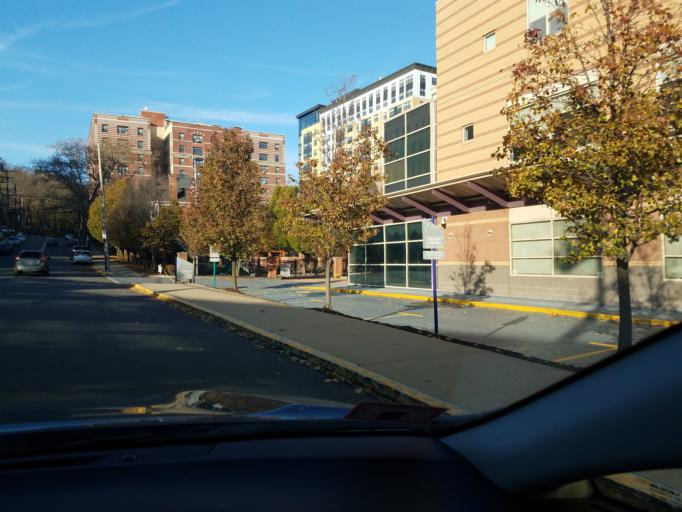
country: US
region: Pennsylvania
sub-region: Allegheny County
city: Bloomfield
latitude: 40.4499
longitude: -79.9533
